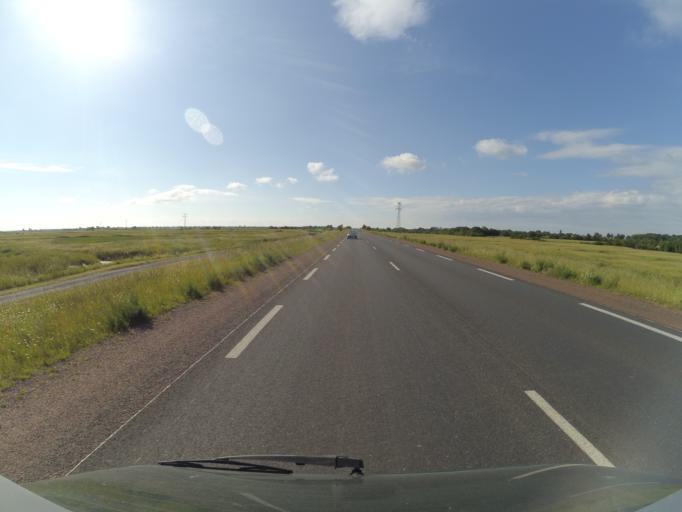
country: FR
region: Poitou-Charentes
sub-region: Departement de la Charente-Maritime
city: Saint-Agnant
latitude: 45.8519
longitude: -0.9590
